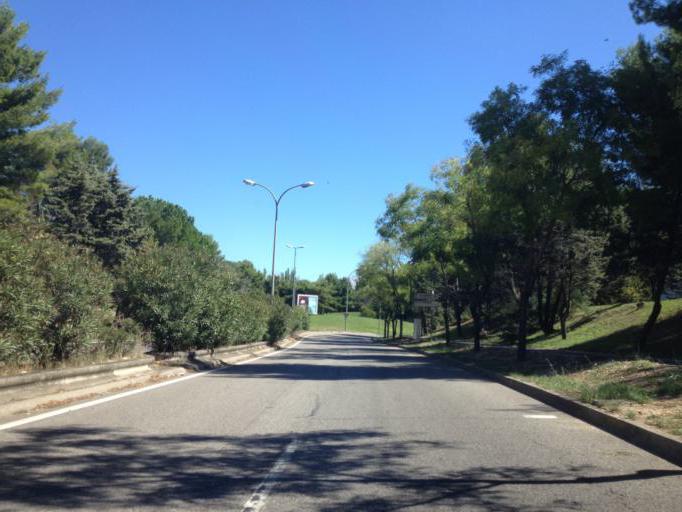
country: FR
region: Provence-Alpes-Cote d'Azur
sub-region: Departement des Bouches-du-Rhone
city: Aix-en-Provence
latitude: 43.5304
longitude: 5.4141
